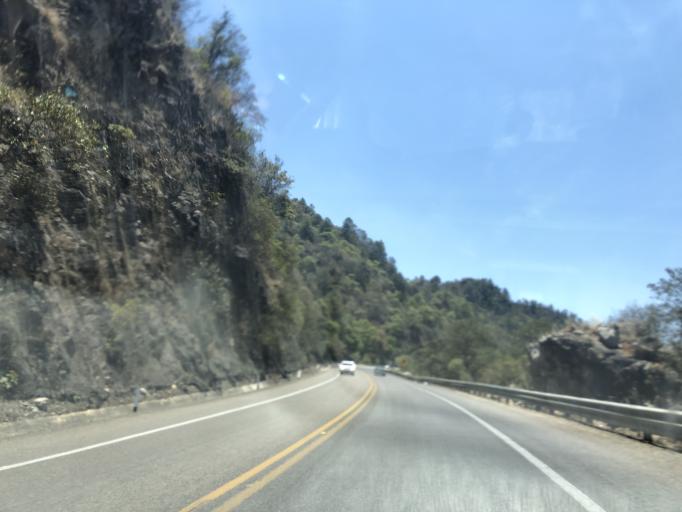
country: MX
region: Chiapas
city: San Cristobal de las Casas
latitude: 16.7205
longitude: -92.6752
